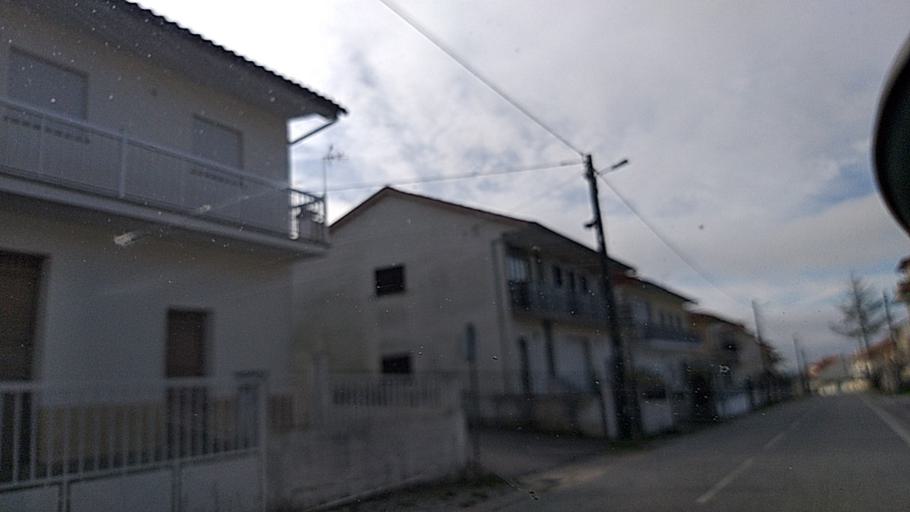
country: PT
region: Guarda
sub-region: Aguiar da Beira
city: Aguiar da Beira
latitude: 40.7817
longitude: -7.5177
